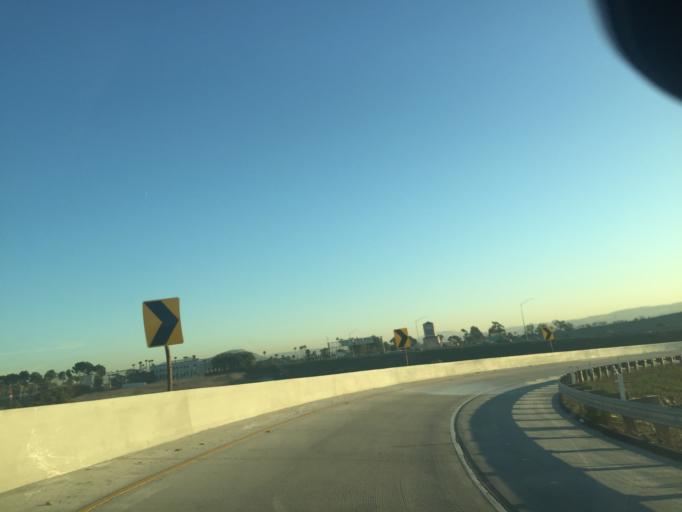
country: MX
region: Baja California
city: Tijuana
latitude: 32.5635
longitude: -116.9452
